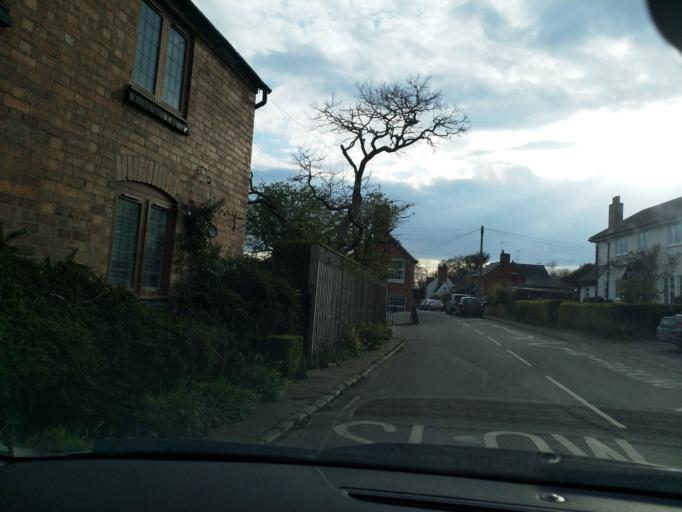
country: GB
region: England
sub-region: Warwickshire
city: Wellesbourne Mountford
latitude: 52.2171
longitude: -1.5553
